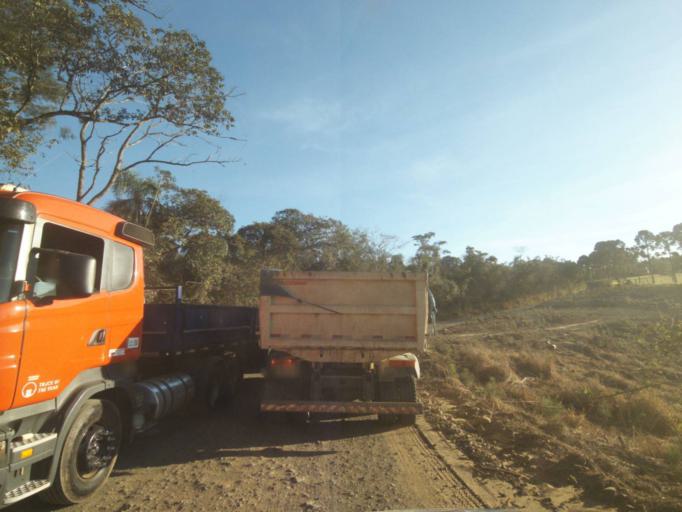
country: BR
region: Parana
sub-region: Telemaco Borba
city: Telemaco Borba
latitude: -24.4264
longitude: -50.5930
